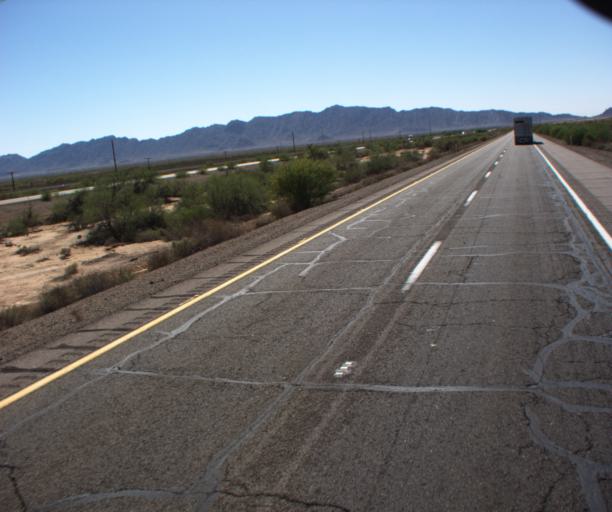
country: US
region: Arizona
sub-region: Yuma County
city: Wellton
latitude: 32.7532
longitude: -113.6559
